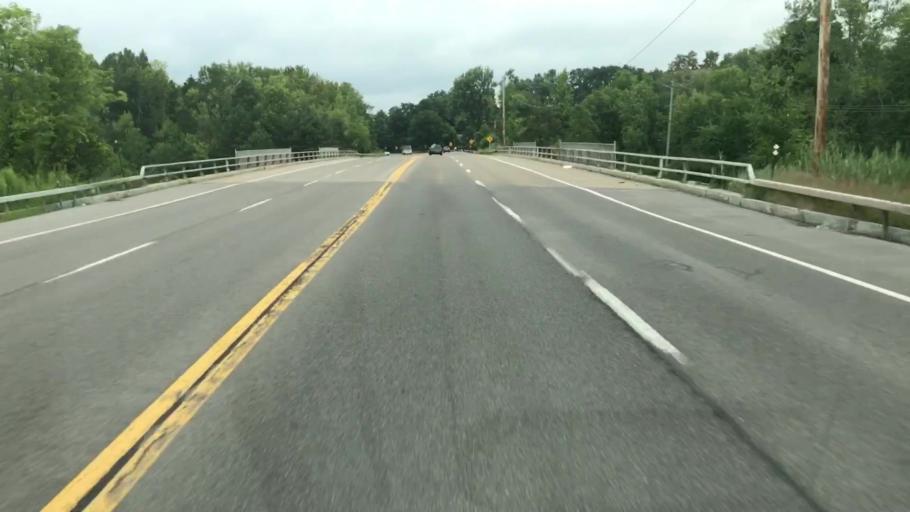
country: US
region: New York
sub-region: Onondaga County
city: Liverpool
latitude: 43.1722
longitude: -76.2092
